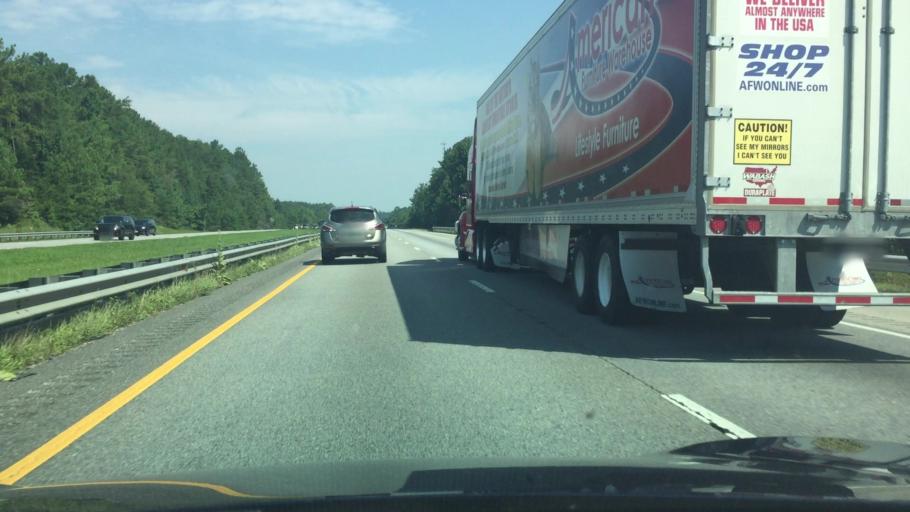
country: US
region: Alabama
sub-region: Shelby County
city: Calera
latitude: 33.0751
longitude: -86.7322
